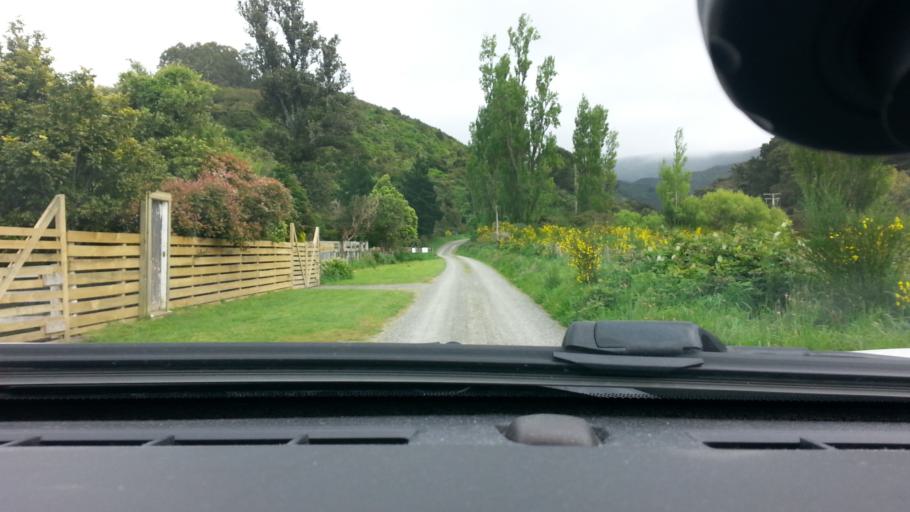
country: NZ
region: Wellington
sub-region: Upper Hutt City
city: Upper Hutt
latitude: -41.1058
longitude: 175.3260
